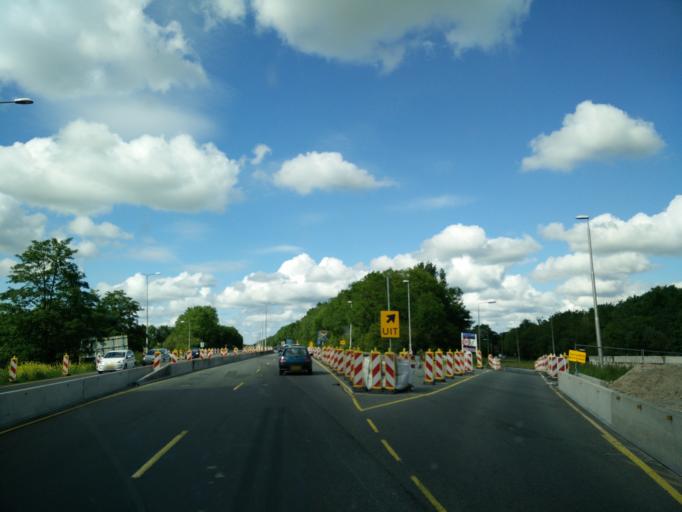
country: NL
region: Groningen
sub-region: Gemeente Groningen
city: Korrewegwijk
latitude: 53.2416
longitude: 6.5691
